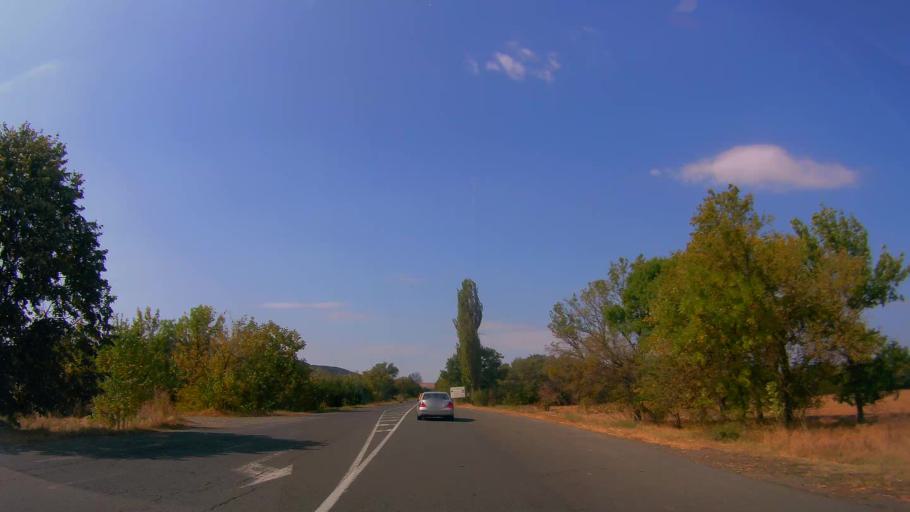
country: BG
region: Burgas
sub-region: Obshtina Karnobat
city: Karnobat
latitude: 42.6573
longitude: 27.0163
